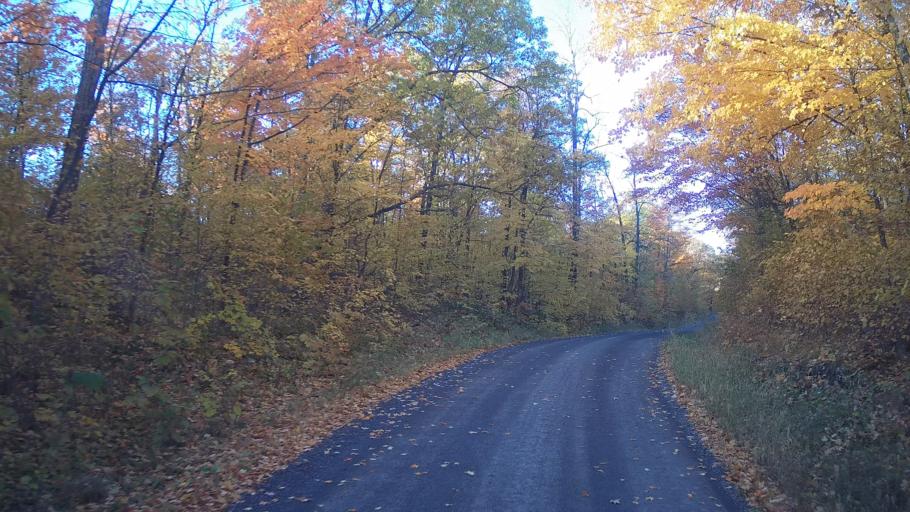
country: CA
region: Ontario
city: Arnprior
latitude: 45.3439
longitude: -76.3427
